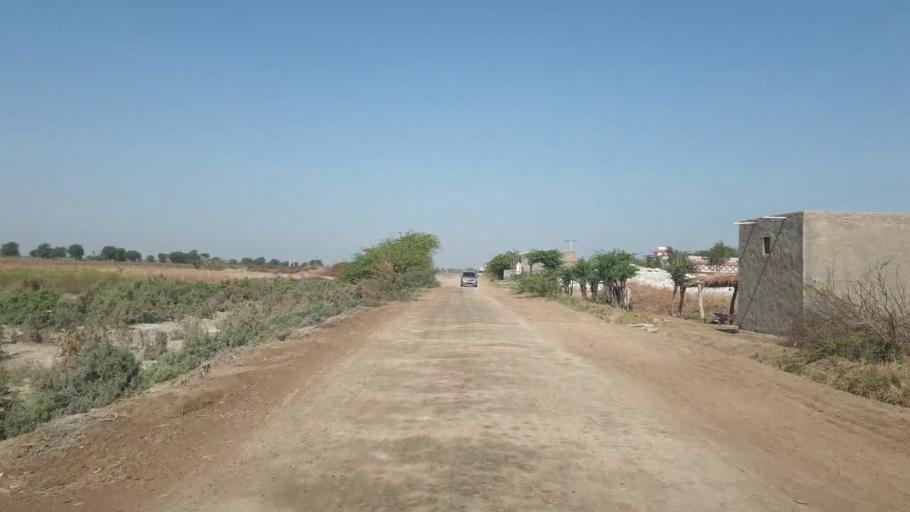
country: PK
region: Sindh
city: Umarkot
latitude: 25.3050
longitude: 69.6158
